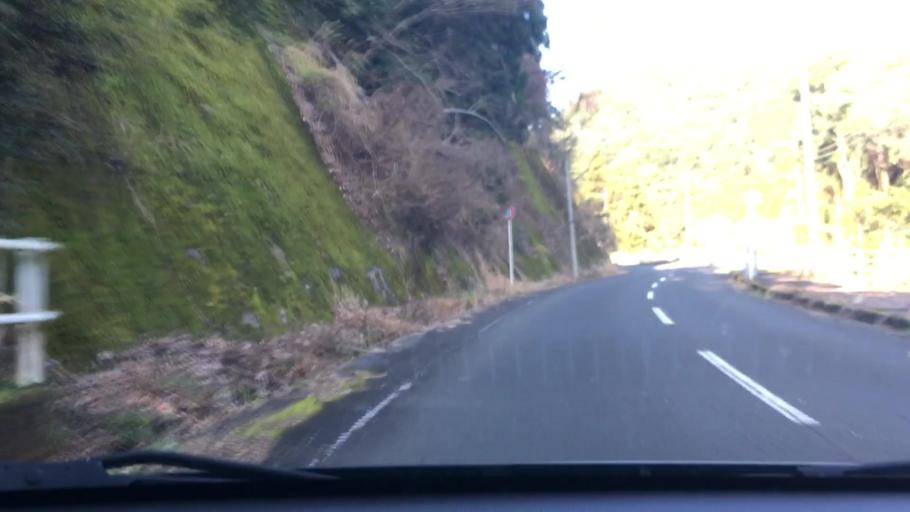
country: JP
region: Kagoshima
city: Satsumasendai
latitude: 31.7519
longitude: 130.4109
